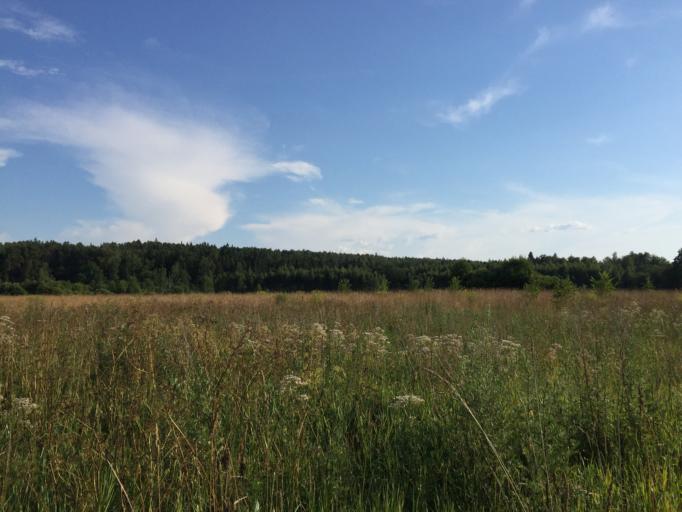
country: LV
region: Krimulda
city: Ragana
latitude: 57.1475
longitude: 24.7588
